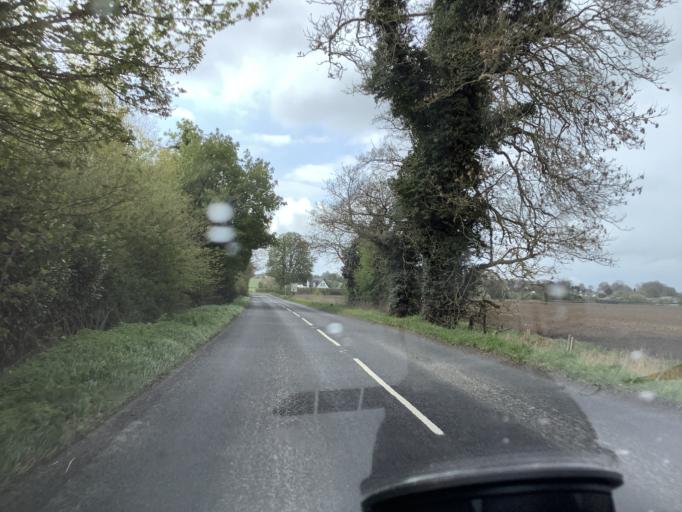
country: GB
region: England
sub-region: Borough of Swindon
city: Wroughton
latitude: 51.4945
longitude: -1.8376
